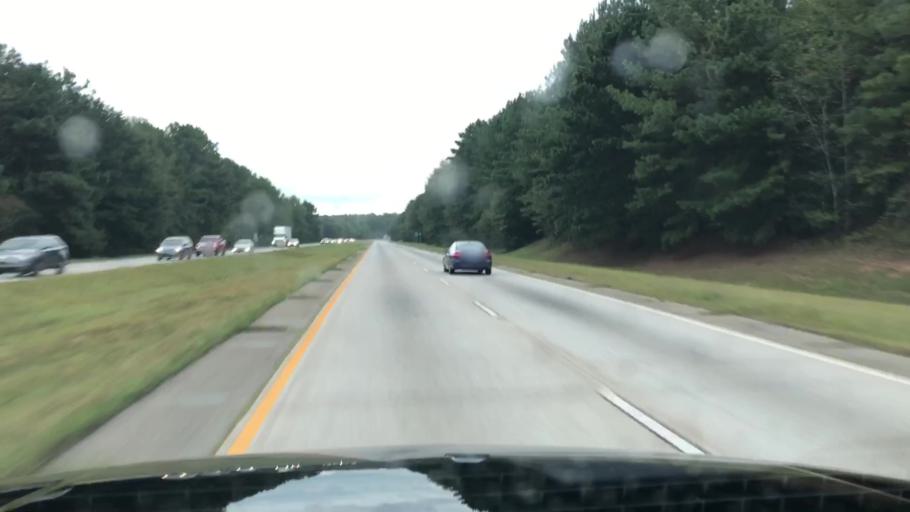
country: US
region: Georgia
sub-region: Cobb County
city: Mableton
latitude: 33.7109
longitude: -84.5766
